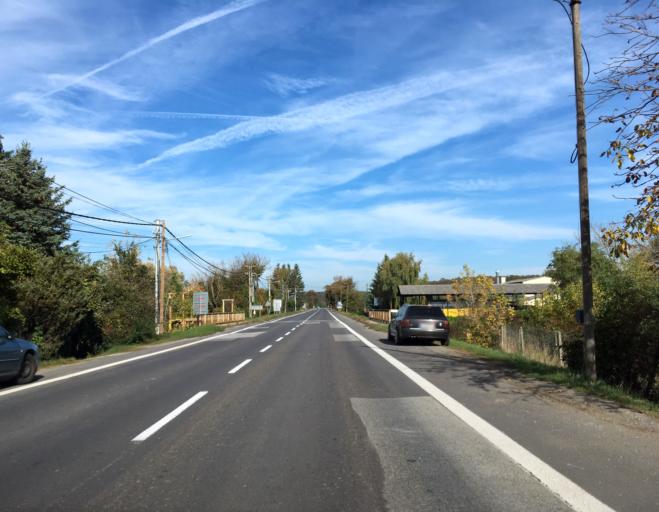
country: SK
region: Banskobystricky
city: Dudince
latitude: 48.1563
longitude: 18.8703
